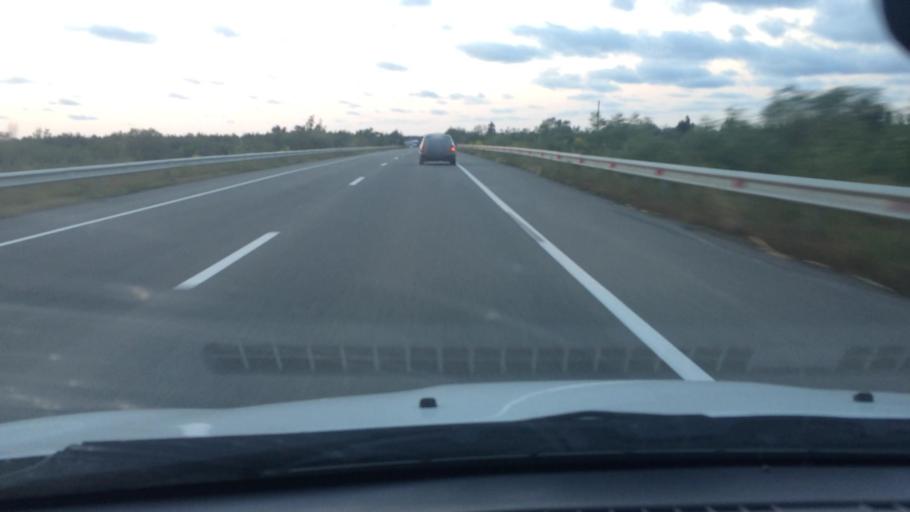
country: GE
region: Ajaria
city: Ochkhamuri
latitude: 41.9066
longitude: 41.7873
